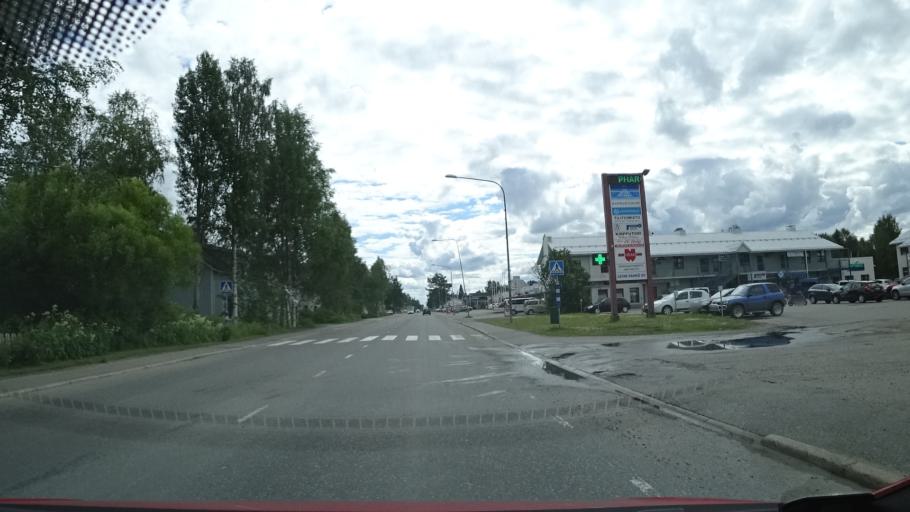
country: FI
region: Lapland
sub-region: Tunturi-Lappi
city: Kittilae
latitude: 67.6584
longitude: 24.9065
